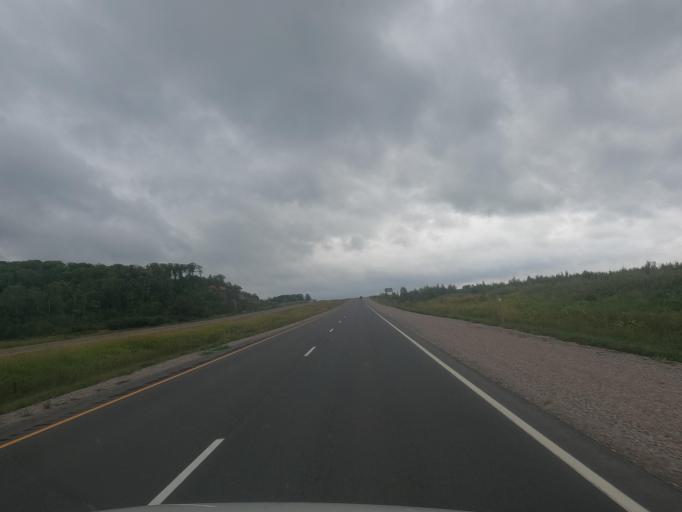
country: CA
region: Ontario
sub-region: Algoma
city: Sault Ste. Marie
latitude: 46.4646
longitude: -84.0592
